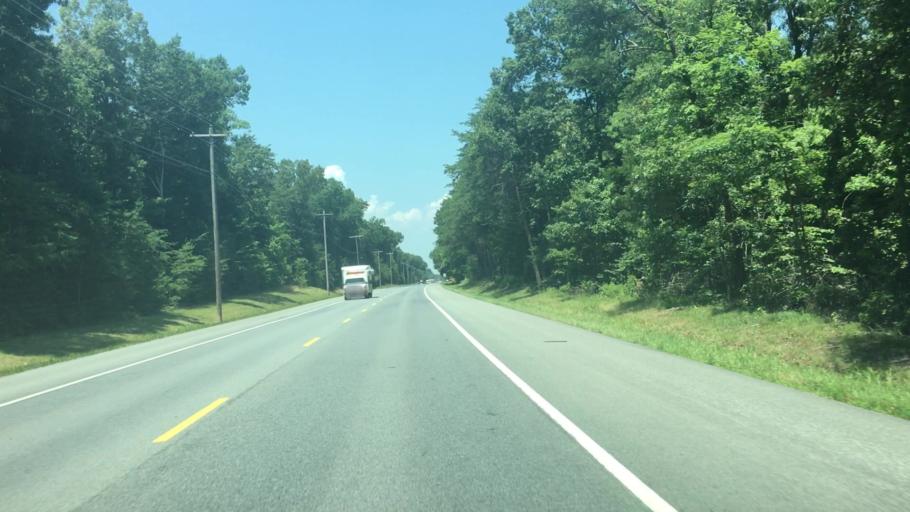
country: US
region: Maryland
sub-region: Saint Mary's County
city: Mechanicsville
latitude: 38.3817
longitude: -76.8182
